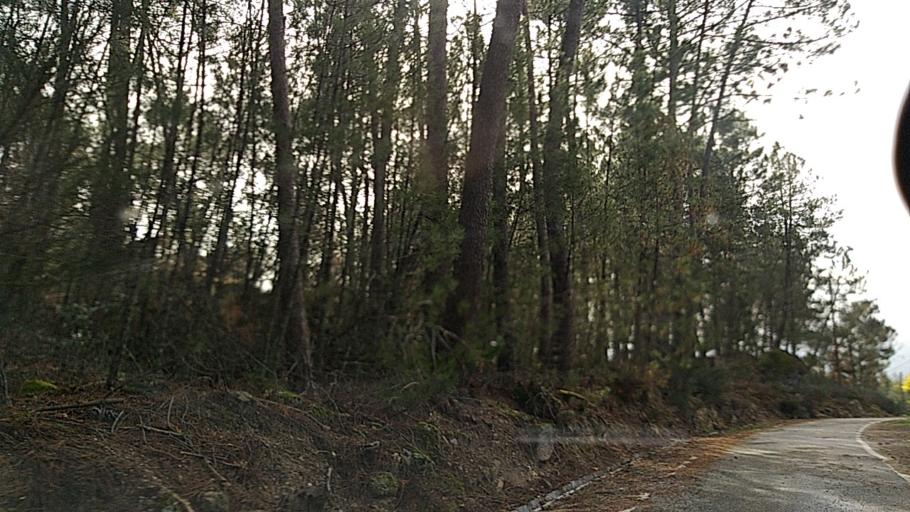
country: PT
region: Guarda
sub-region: Fornos de Algodres
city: Fornos de Algodres
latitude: 40.6345
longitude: -7.5381
